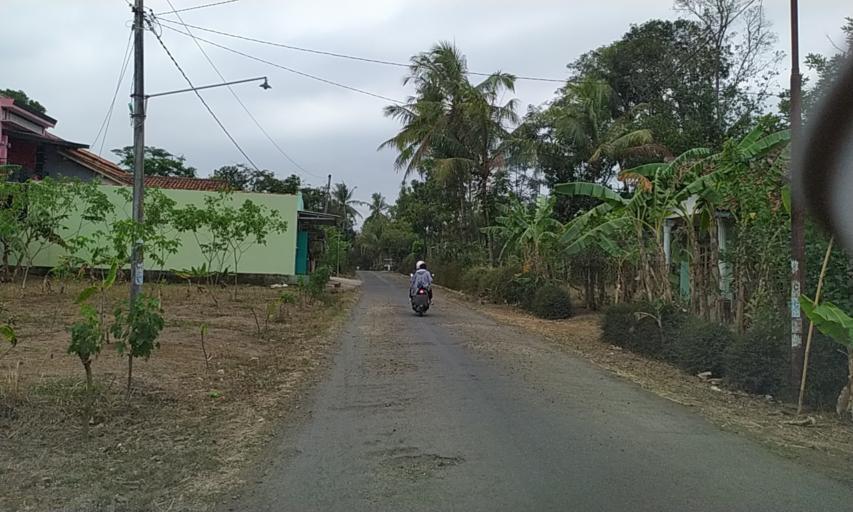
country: ID
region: Central Java
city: Kroya
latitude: -7.6488
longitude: 109.2498
